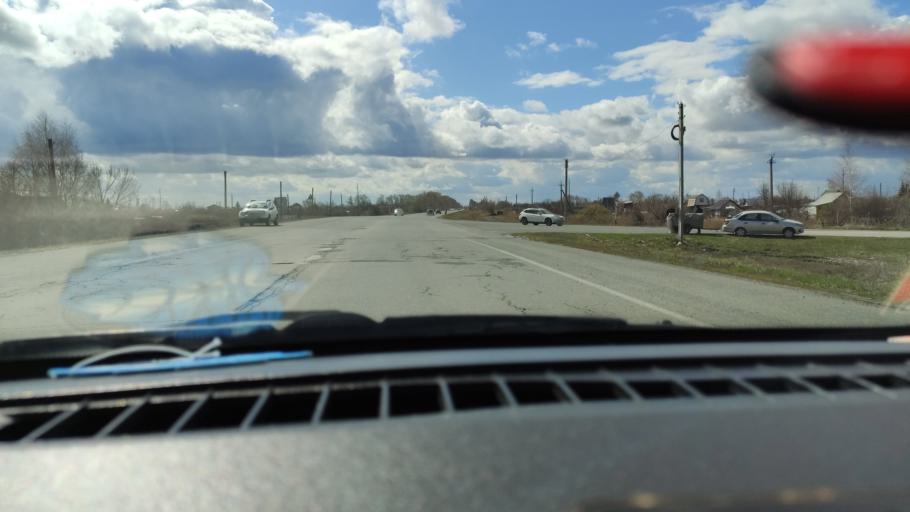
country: RU
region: Samara
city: Tol'yatti
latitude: 53.7100
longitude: 49.4232
